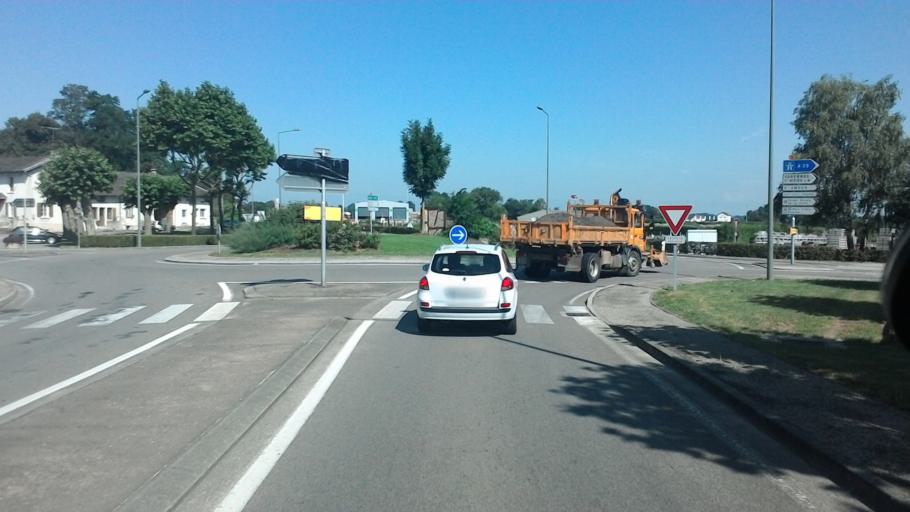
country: FR
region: Rhone-Alpes
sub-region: Departement de l'Ain
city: Saint-Trivier-de-Courtes
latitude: 46.4600
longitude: 5.0836
